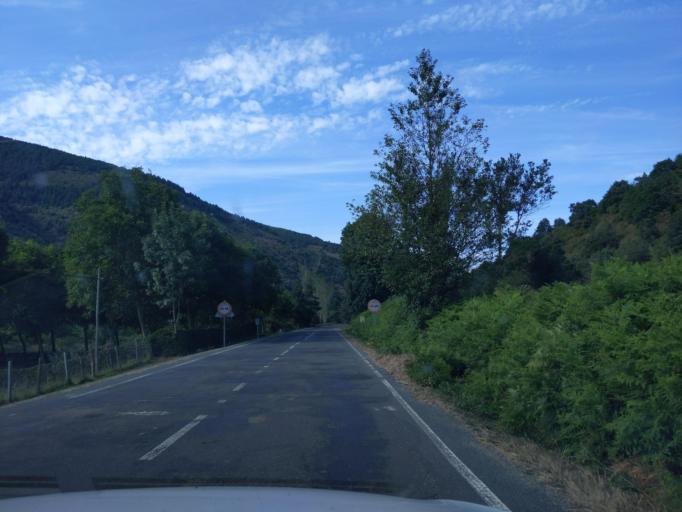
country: ES
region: La Rioja
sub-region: Provincia de La Rioja
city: Ezcaray
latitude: 42.2968
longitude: -3.0251
